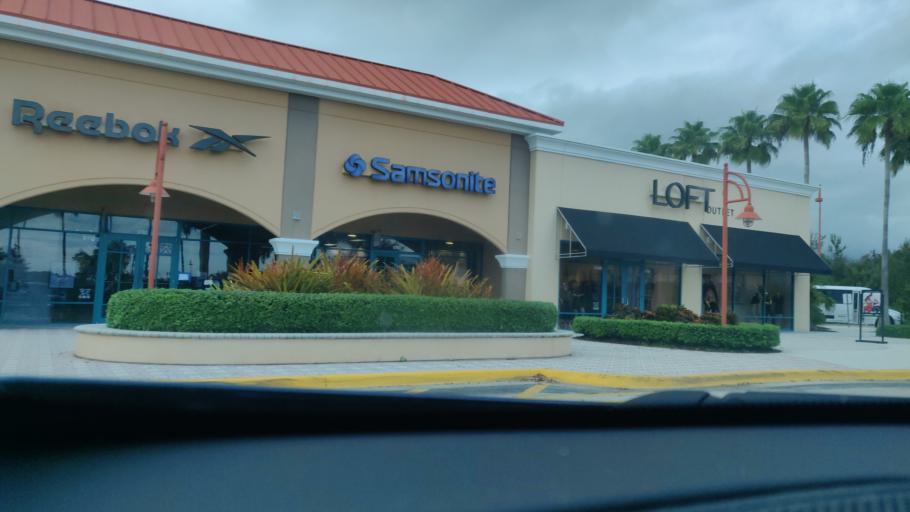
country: US
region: Florida
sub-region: Indian River County
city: West Vero Corridor
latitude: 27.6361
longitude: -80.5225
